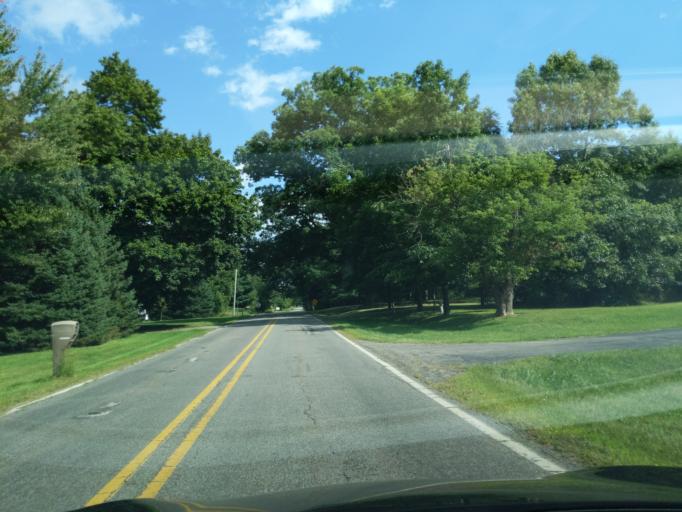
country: US
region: Michigan
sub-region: Jackson County
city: Spring Arbor
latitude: 42.2995
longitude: -84.5016
